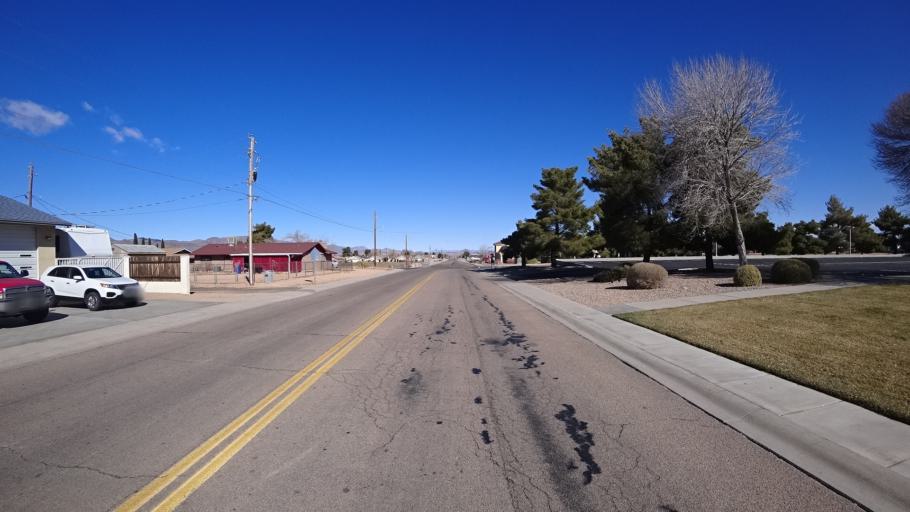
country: US
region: Arizona
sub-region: Mohave County
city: Kingman
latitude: 35.1952
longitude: -114.0114
